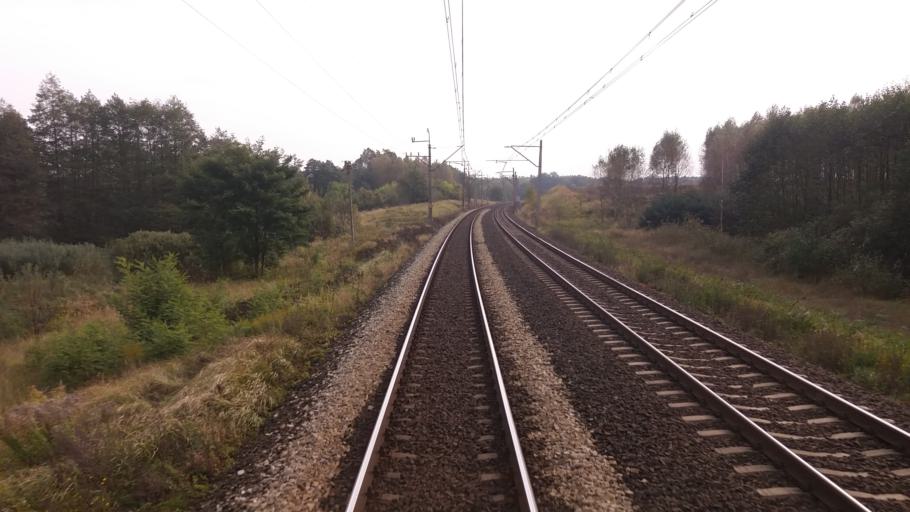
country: PL
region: West Pomeranian Voivodeship
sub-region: Powiat stargardzki
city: Dolice
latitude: 53.1806
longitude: 15.2759
